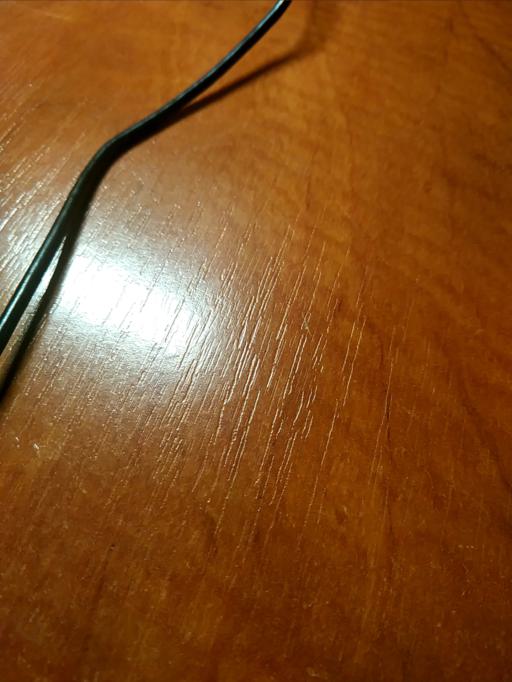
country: RU
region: Tverskaya
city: Vyshniy Volochek
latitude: 57.3915
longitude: 34.5318
